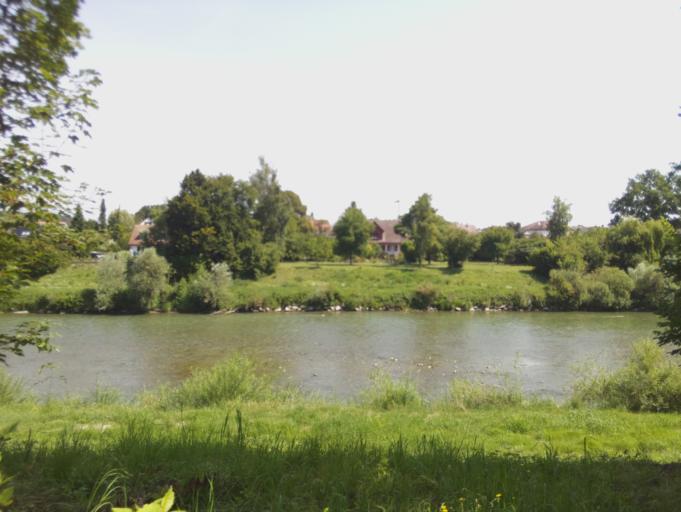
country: CH
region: Zurich
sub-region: Bezirk Andelfingen
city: Grossandelfingen
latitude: 47.5974
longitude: 8.6791
